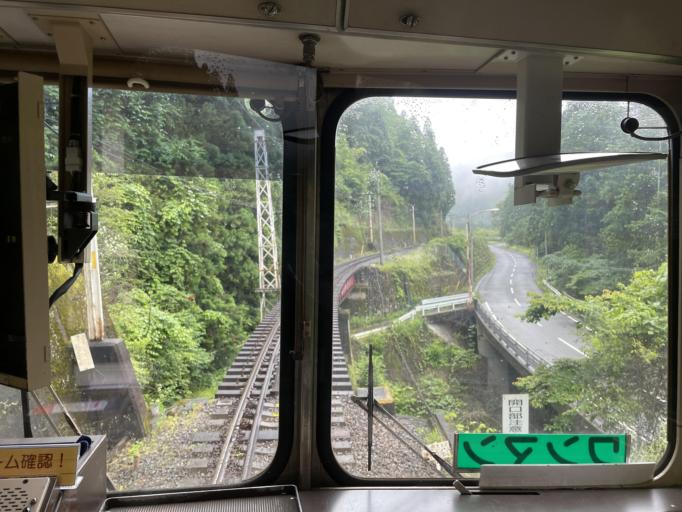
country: JP
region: Saitama
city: Chichibu
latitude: 35.9567
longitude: 139.0038
